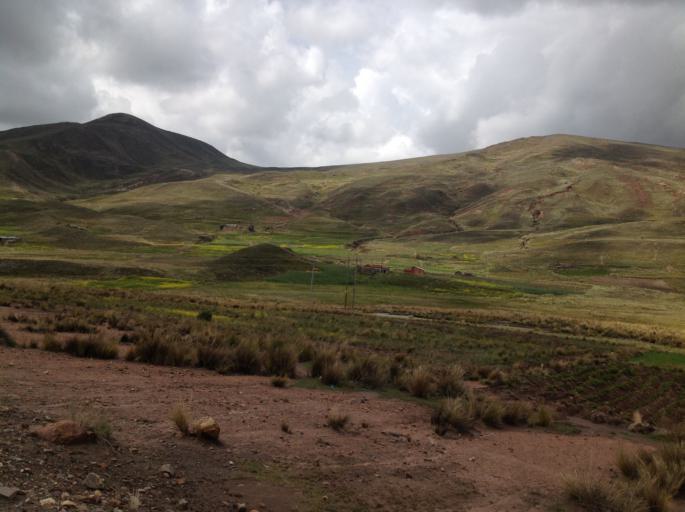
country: BO
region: La Paz
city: Yumani
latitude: -15.7690
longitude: -68.9797
